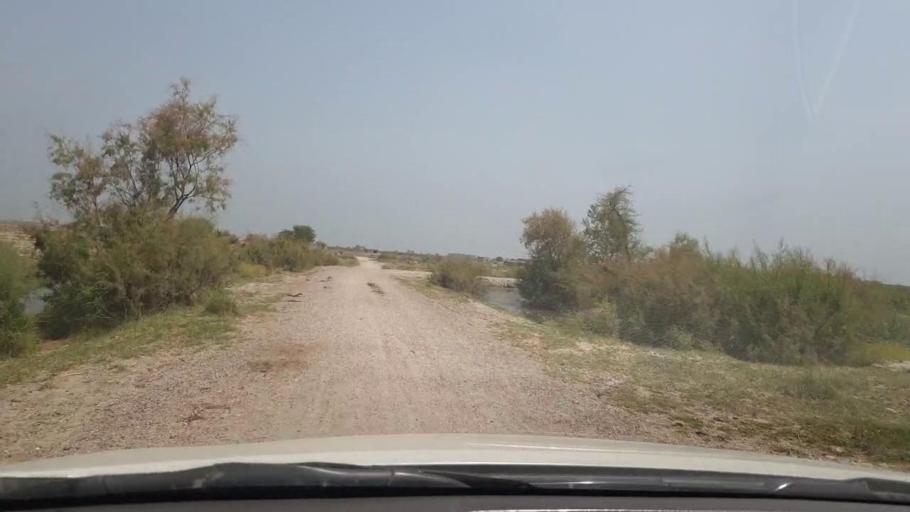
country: PK
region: Sindh
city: Shikarpur
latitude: 28.0295
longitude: 68.6486
